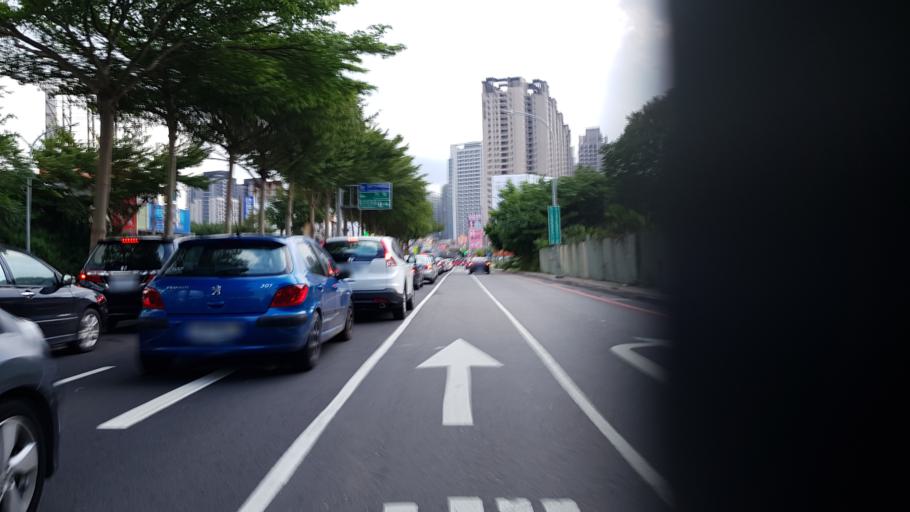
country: TW
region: Taiwan
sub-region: Hsinchu
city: Zhubei
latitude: 24.7976
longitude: 121.0133
